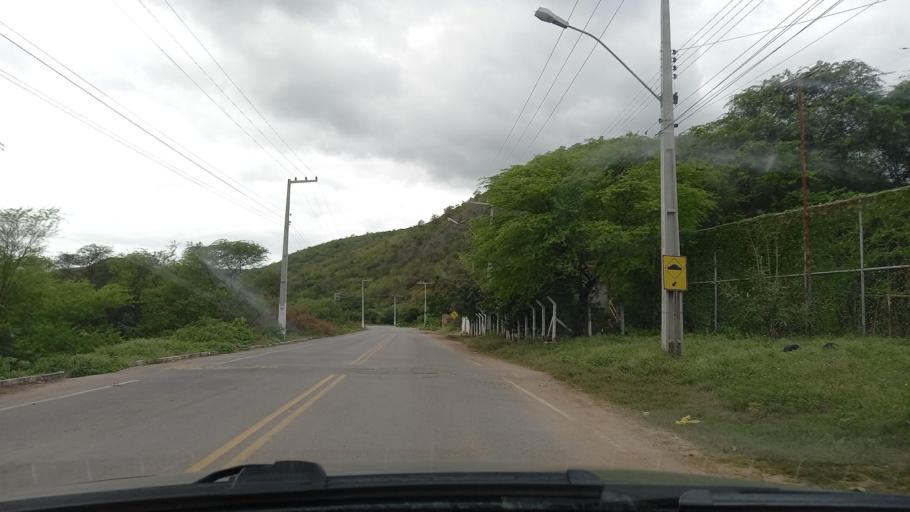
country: BR
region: Sergipe
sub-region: Caninde De Sao Francisco
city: Caninde de Sao Francisco
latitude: -9.6426
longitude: -37.7806
